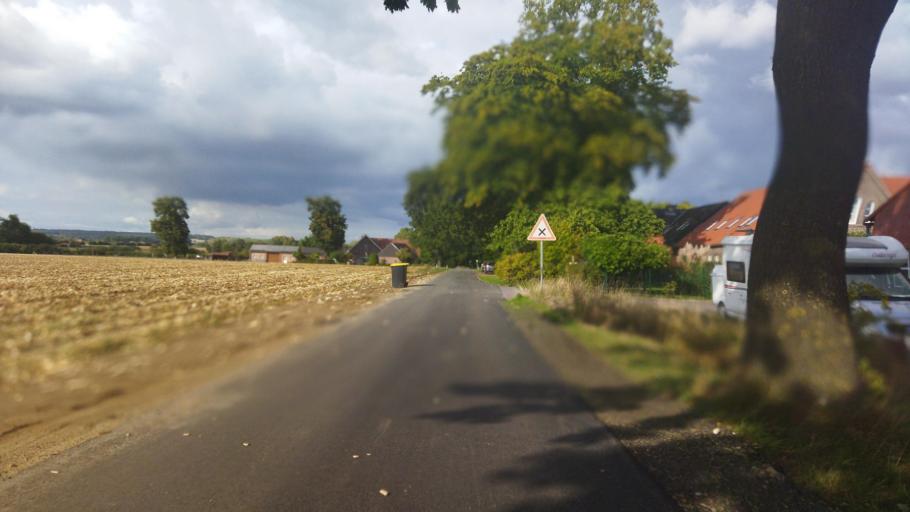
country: DE
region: North Rhine-Westphalia
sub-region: Regierungsbezirk Munster
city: Dulmen
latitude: 51.8705
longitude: 7.2616
